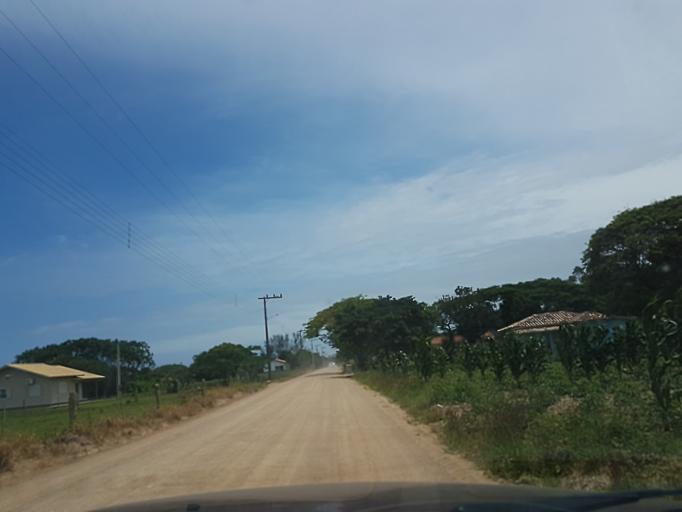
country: BR
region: Santa Catarina
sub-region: Jaguaruna
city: Jaguaruna
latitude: -28.6417
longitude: -48.9638
